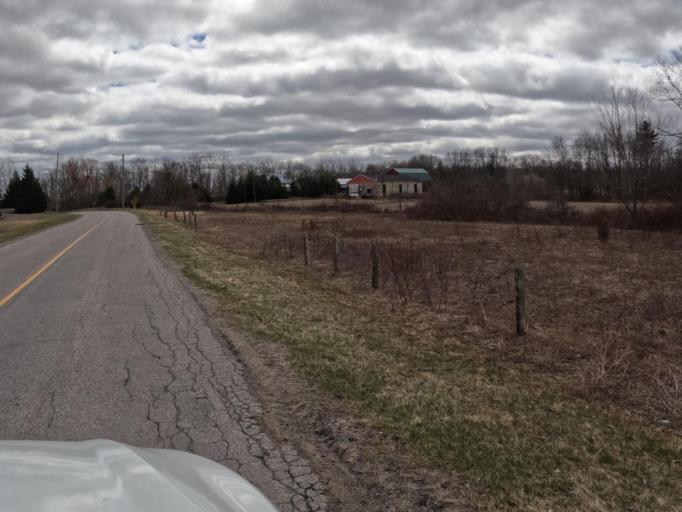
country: CA
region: Ontario
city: Norfolk County
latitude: 42.8012
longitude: -80.3656
